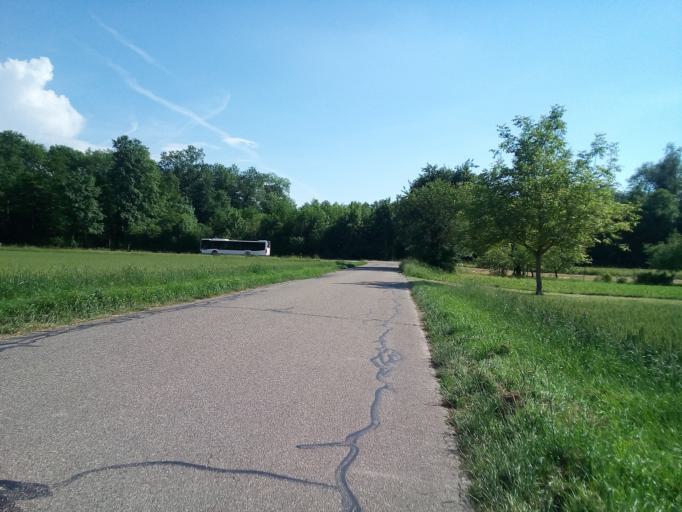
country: DE
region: Baden-Wuerttemberg
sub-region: Karlsruhe Region
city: Lichtenau
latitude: 48.7308
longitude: 7.9825
